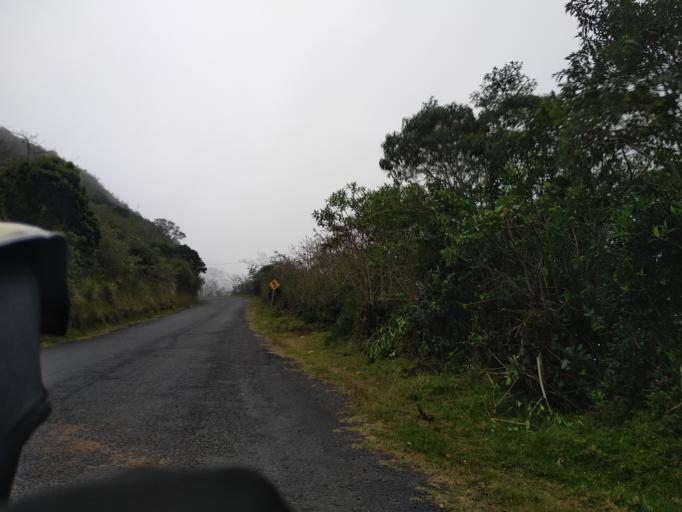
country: EC
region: Cotopaxi
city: Saquisili
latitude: -0.6851
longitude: -78.8338
